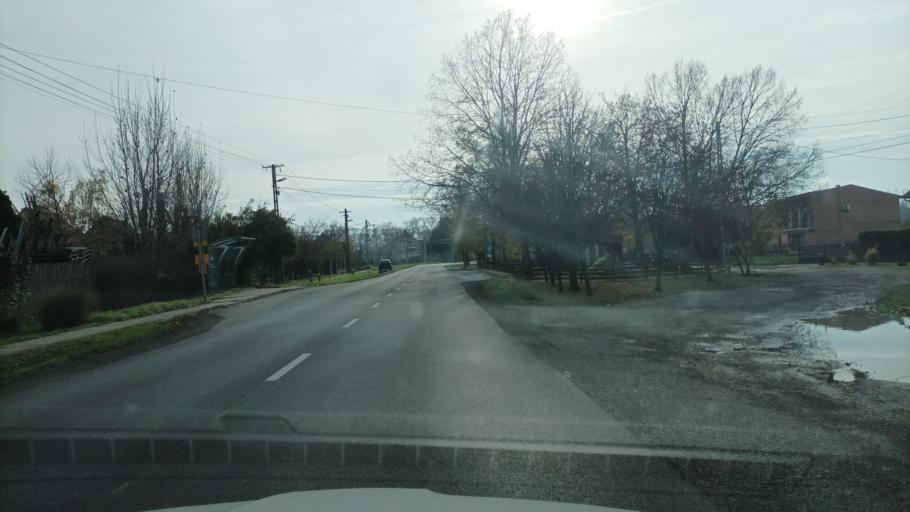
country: HU
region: Pest
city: Rackeve
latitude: 47.1430
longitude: 18.9471
